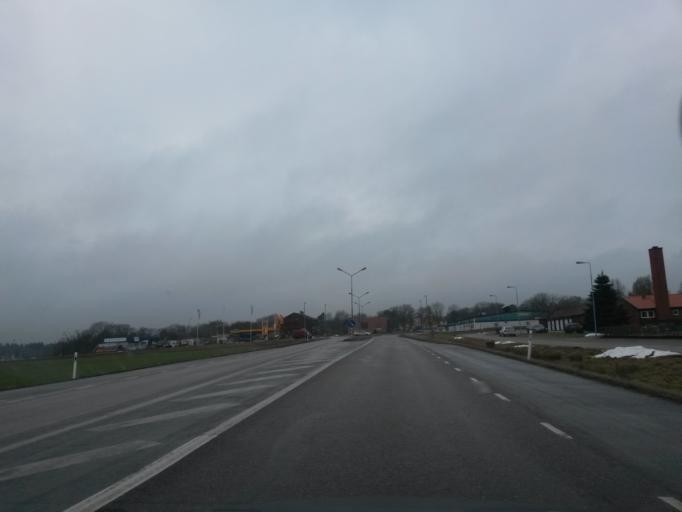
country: SE
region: Vaestra Goetaland
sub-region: Vanersborgs Kommun
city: Vargon
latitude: 58.3515
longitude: 12.3949
